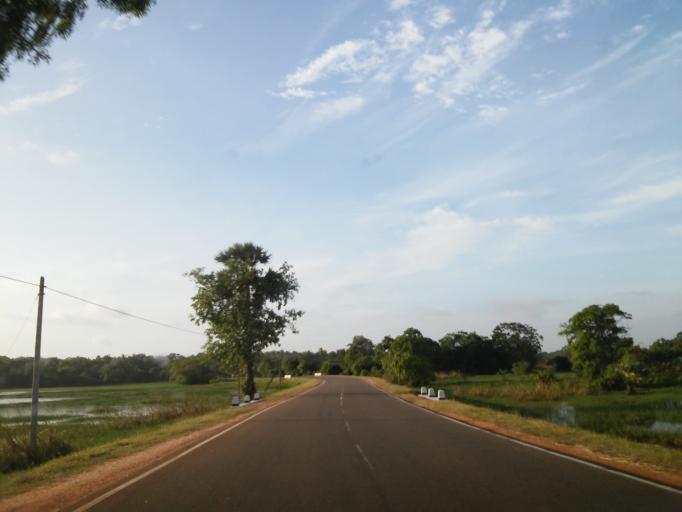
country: LK
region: Central
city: Sigiriya
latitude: 8.1134
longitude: 80.5816
